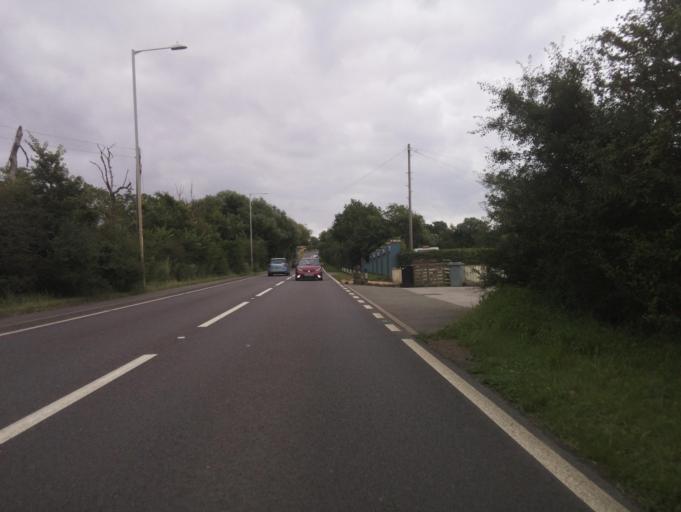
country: GB
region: England
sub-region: Lincolnshire
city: Barrowby
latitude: 52.9244
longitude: -0.6955
